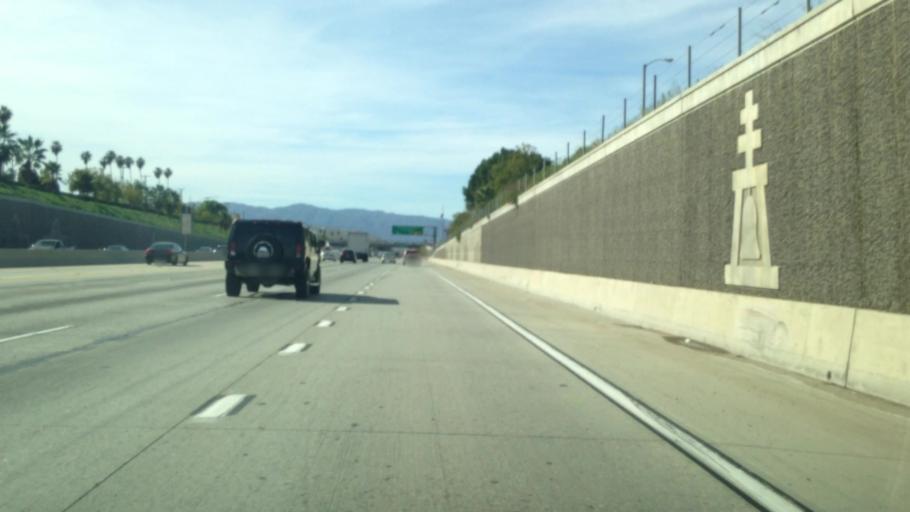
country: US
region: California
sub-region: Riverside County
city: Riverside
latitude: 33.9182
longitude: -117.4364
